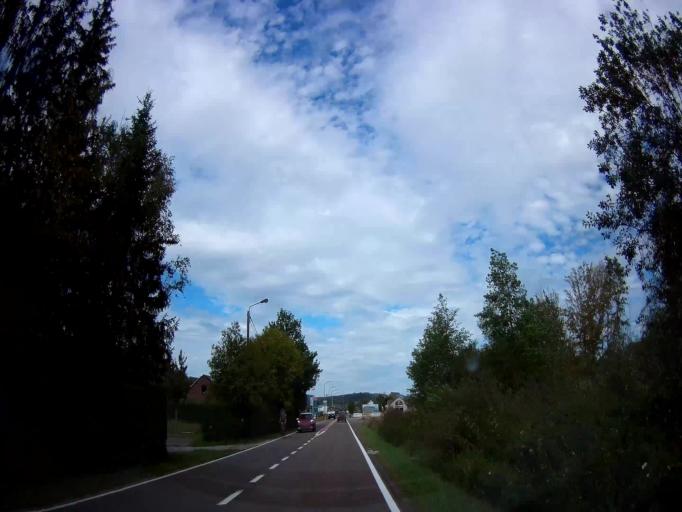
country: BE
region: Wallonia
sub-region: Province du Luxembourg
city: Durbuy
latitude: 50.3395
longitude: 5.4848
